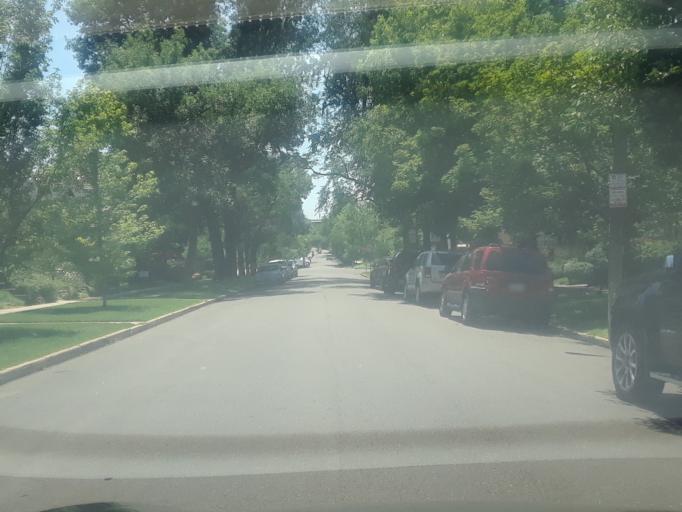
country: US
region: Colorado
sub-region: Arapahoe County
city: Glendale
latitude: 39.7251
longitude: -104.9534
